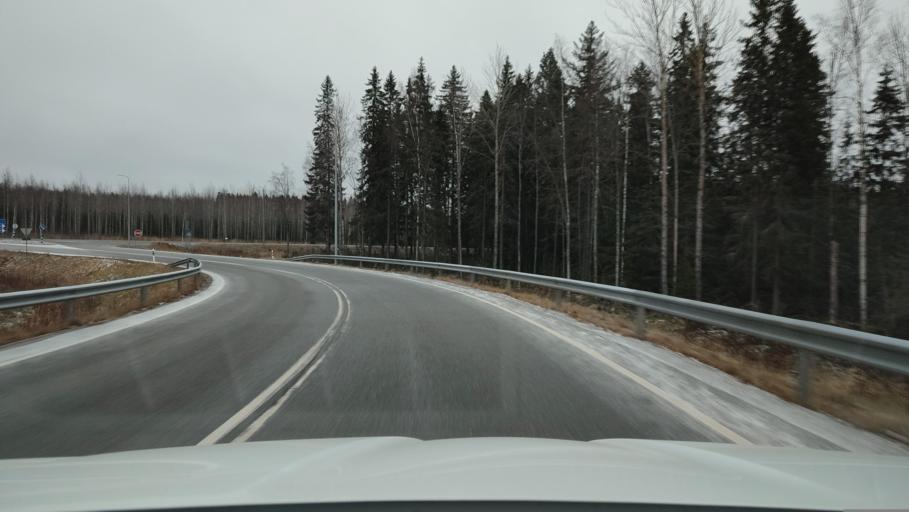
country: FI
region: Ostrobothnia
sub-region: Sydosterbotten
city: Naerpes
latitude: 62.4102
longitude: 21.4146
